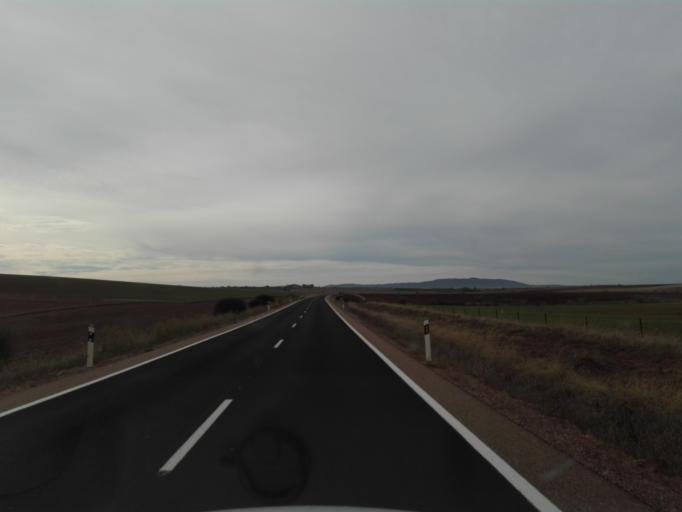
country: ES
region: Extremadura
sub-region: Provincia de Badajoz
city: Valencia de las Torres
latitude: 38.3379
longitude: -5.9642
